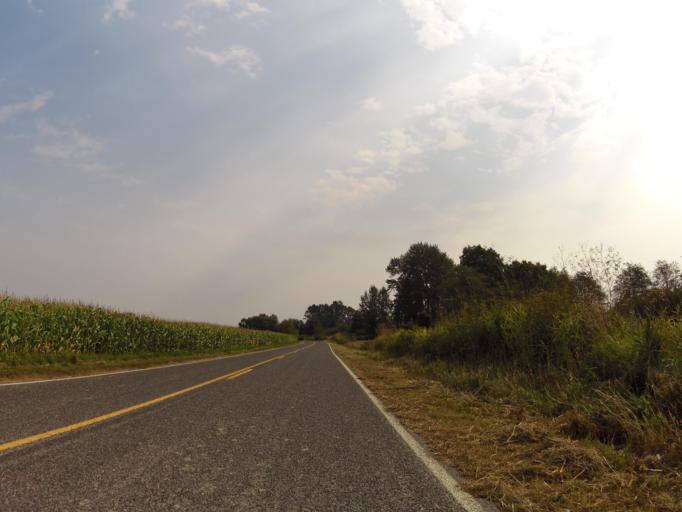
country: US
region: Washington
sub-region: Whatcom County
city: Ferndale
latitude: 48.8086
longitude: -122.6323
